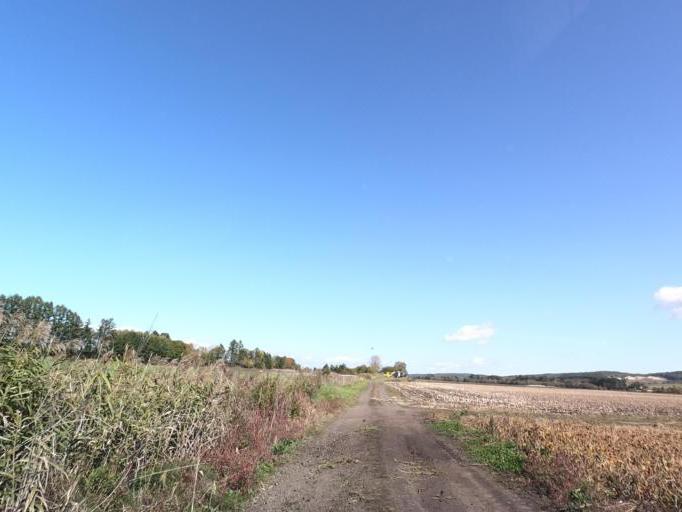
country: JP
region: Hokkaido
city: Otofuke
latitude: 43.0624
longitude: 143.2781
